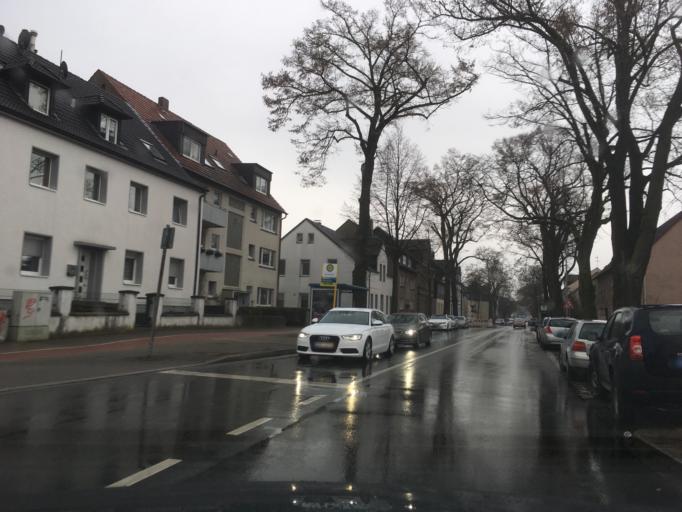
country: DE
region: North Rhine-Westphalia
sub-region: Regierungsbezirk Arnsberg
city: Herne
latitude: 51.5567
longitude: 7.2105
